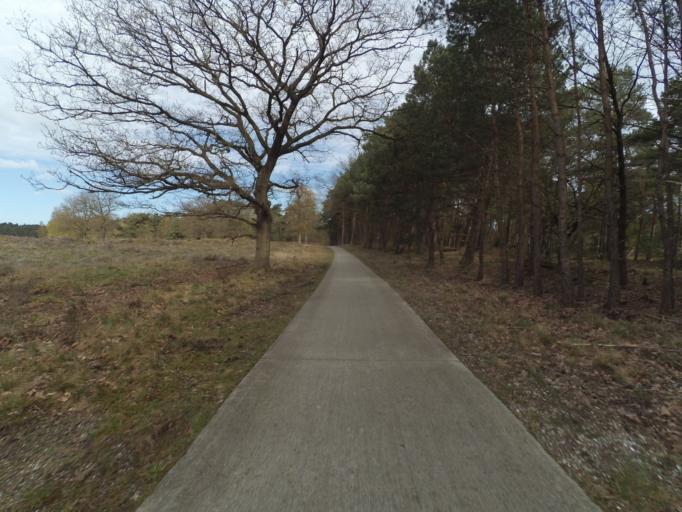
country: NL
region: Gelderland
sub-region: Gemeente Nunspeet
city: Nunspeet
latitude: 52.3501
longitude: 5.7635
